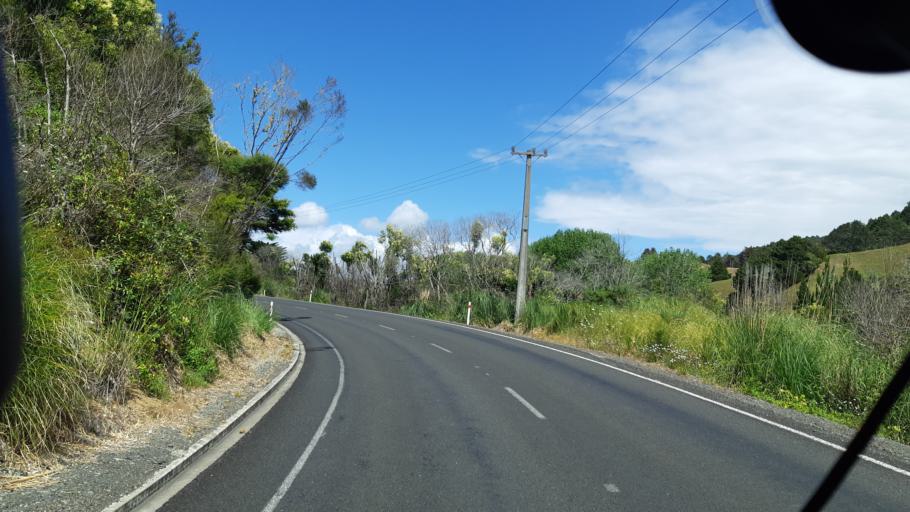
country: NZ
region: Northland
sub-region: Far North District
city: Taipa
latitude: -35.2673
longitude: 173.4976
